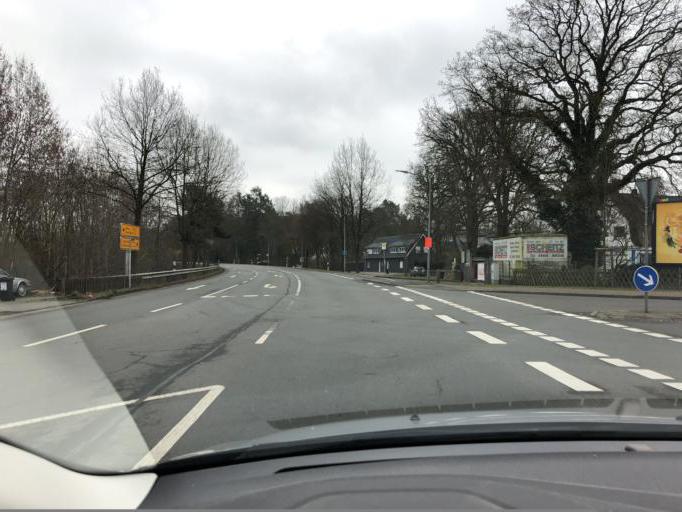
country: DE
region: Lower Saxony
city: Hude
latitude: 53.1019
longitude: 8.4775
